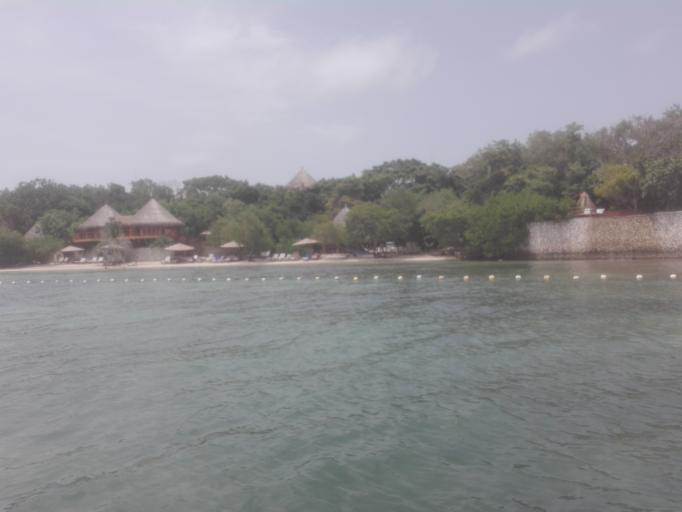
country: CO
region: Bolivar
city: Turbana
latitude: 10.1525
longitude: -75.6877
